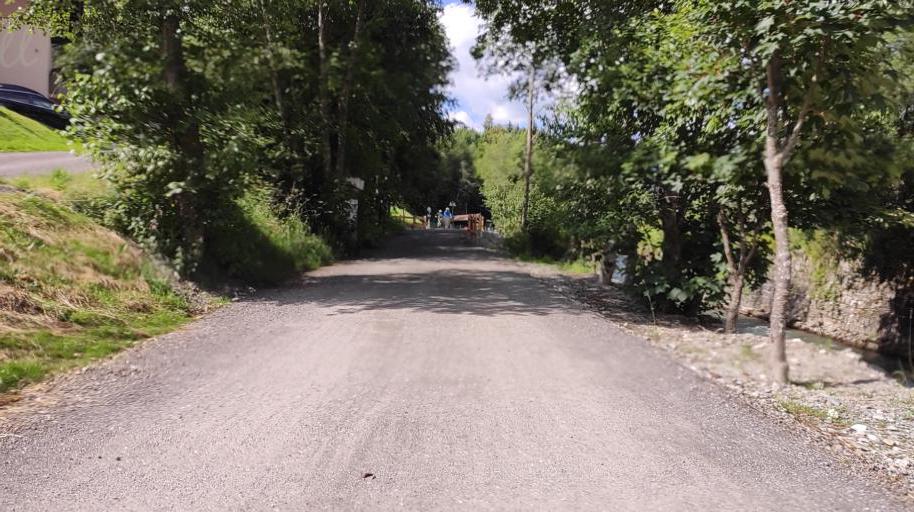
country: AT
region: Salzburg
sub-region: Politischer Bezirk Zell am See
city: Saalbach
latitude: 47.3904
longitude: 12.6283
